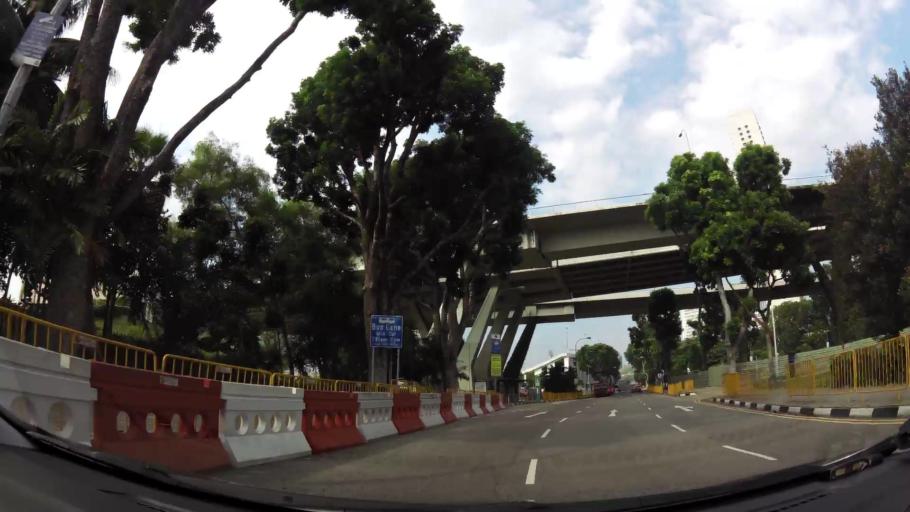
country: SG
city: Singapore
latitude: 1.2894
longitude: 103.8623
